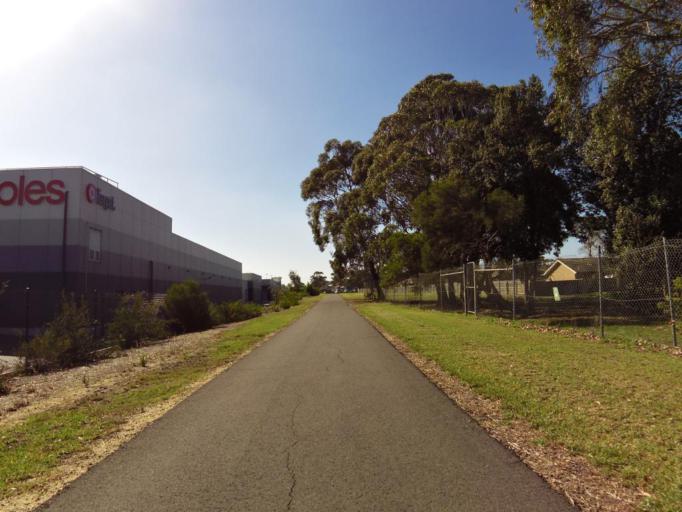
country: AU
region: Victoria
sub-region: Bass Coast
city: North Wonthaggi
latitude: -38.6046
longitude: 145.5848
